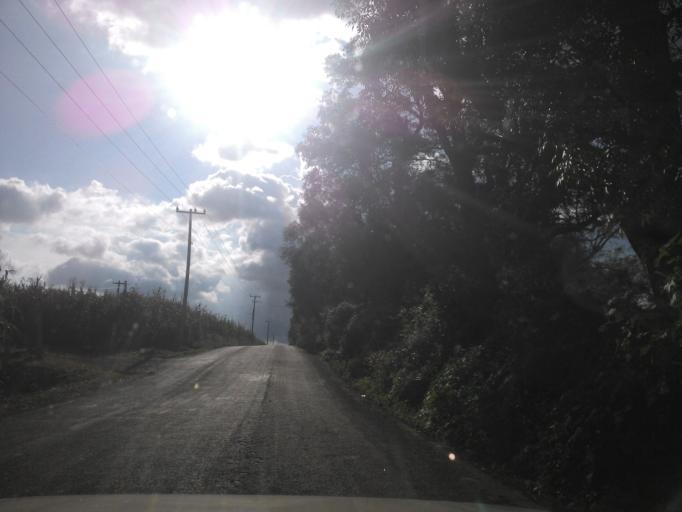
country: MX
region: Jalisco
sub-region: Atotonilco el Alto
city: Ojo de Agua de Moran
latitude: 20.6024
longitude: -102.4835
